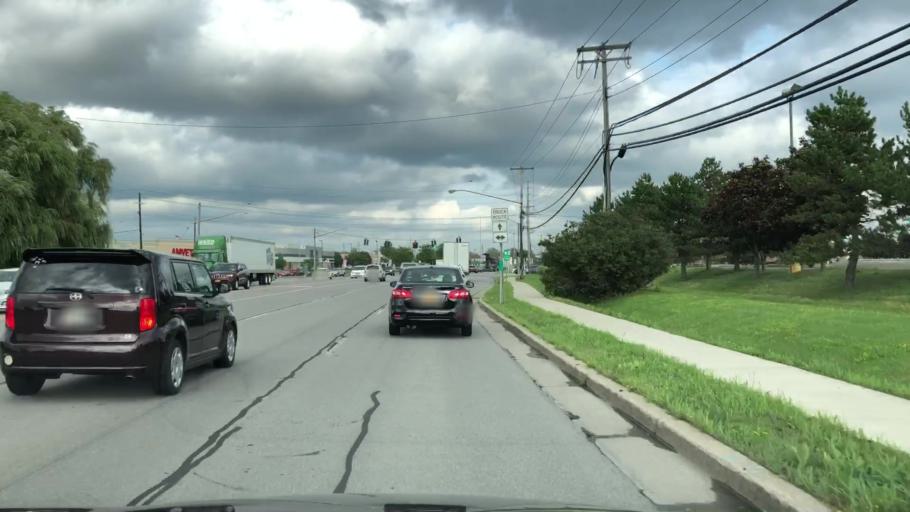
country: US
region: New York
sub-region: Erie County
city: Cheektowaga
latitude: 42.9095
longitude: -78.7318
